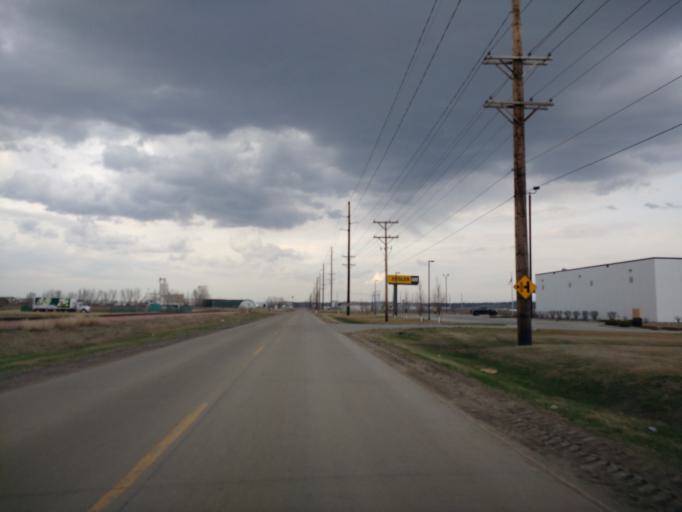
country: US
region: Iowa
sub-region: Woodbury County
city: Sergeant Bluff
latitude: 42.4131
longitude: -96.3700
